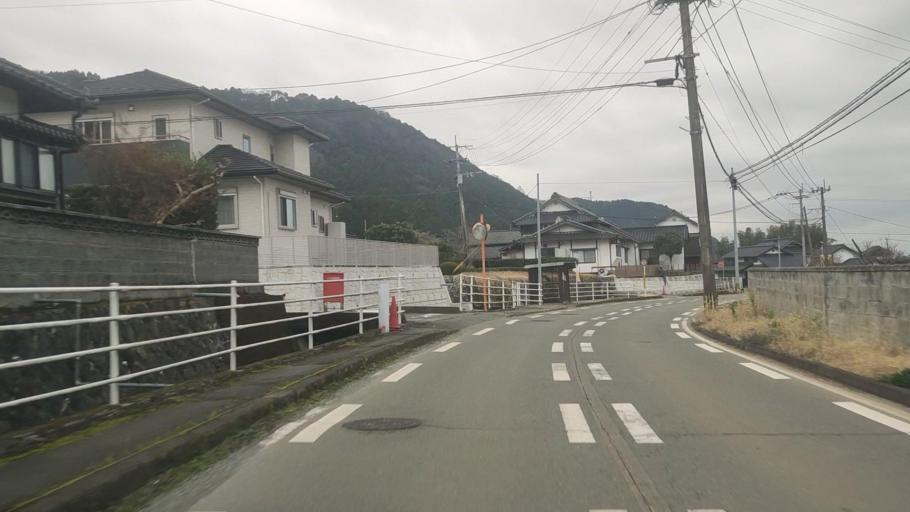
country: JP
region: Kumamoto
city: Ozu
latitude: 32.8540
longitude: 130.8793
